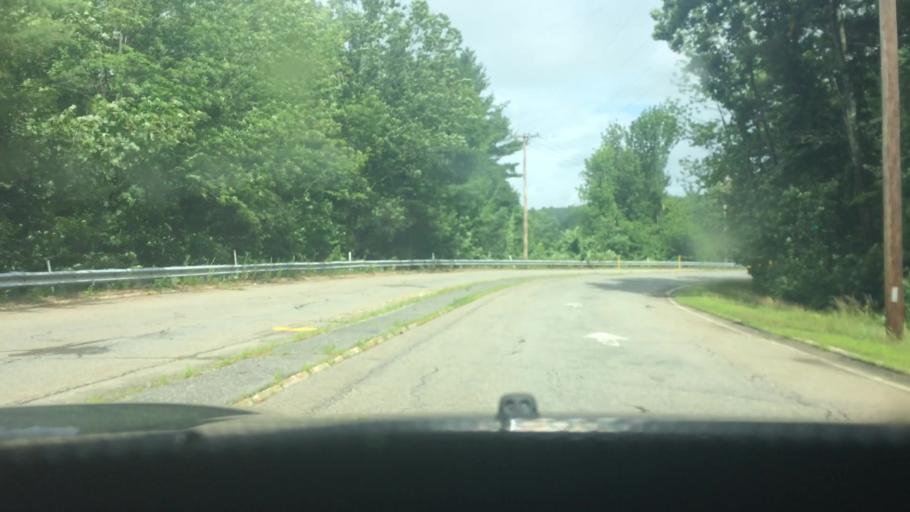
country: US
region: Massachusetts
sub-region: Worcester County
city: Athol
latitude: 42.5789
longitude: -72.1812
